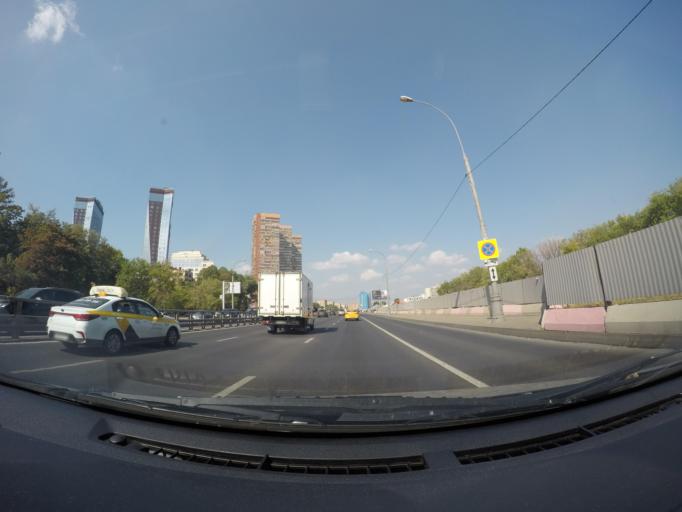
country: RU
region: Moscow
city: Novovladykino
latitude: 55.8160
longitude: 37.5764
